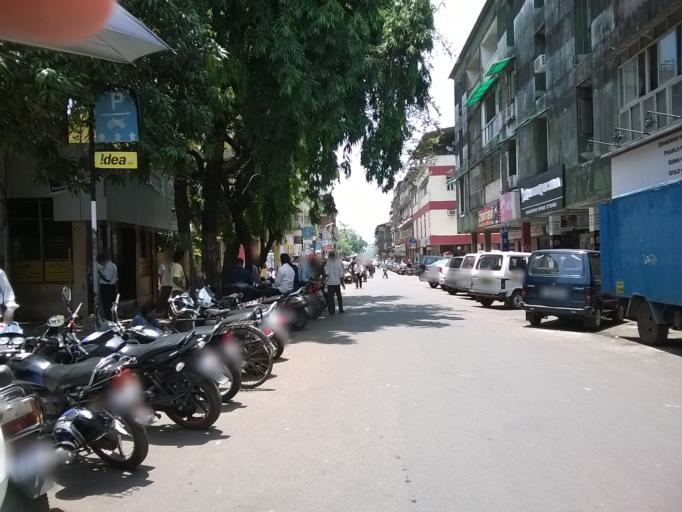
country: IN
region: Goa
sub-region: North Goa
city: Panaji
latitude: 15.4982
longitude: 73.8232
